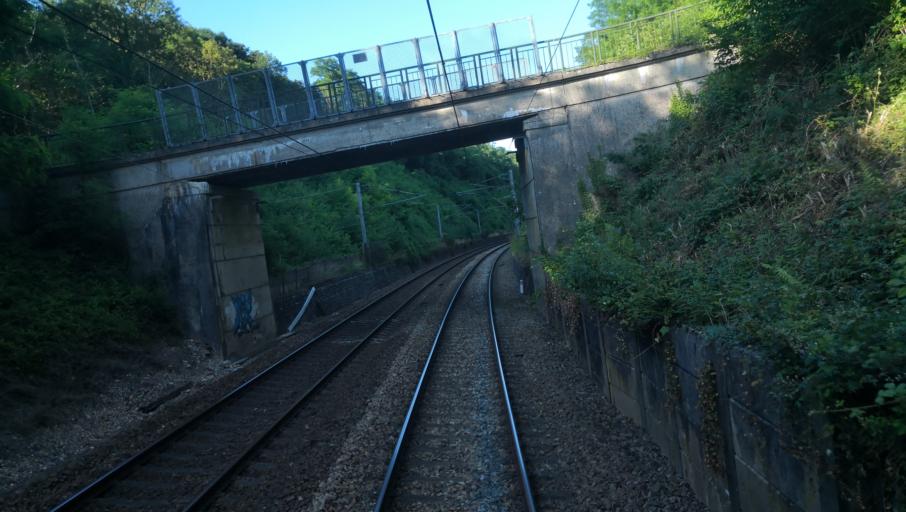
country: FR
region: Ile-de-France
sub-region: Departement des Yvelines
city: Rosny-sur-Seine
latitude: 48.9829
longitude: 1.6241
